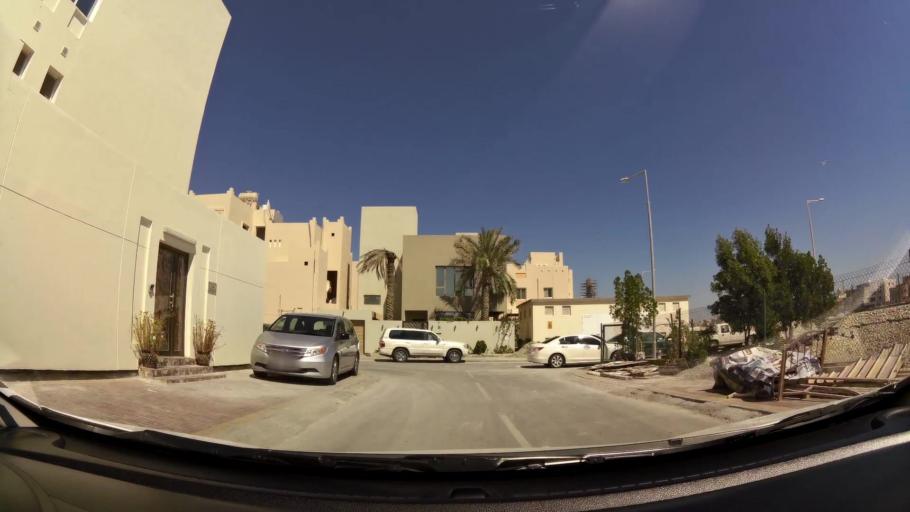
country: BH
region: Muharraq
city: Al Muharraq
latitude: 26.2742
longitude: 50.5983
